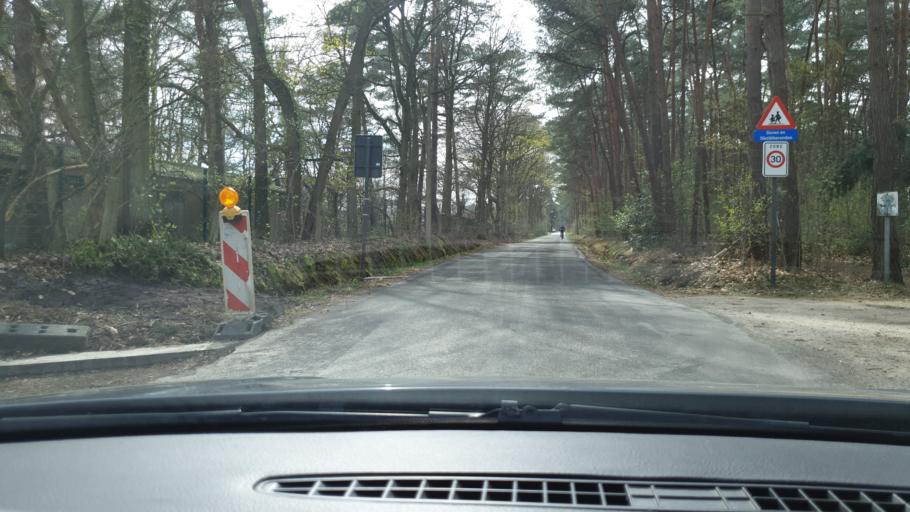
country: BE
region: Flanders
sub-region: Provincie Limburg
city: Zonhoven
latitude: 50.9535
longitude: 5.3756
